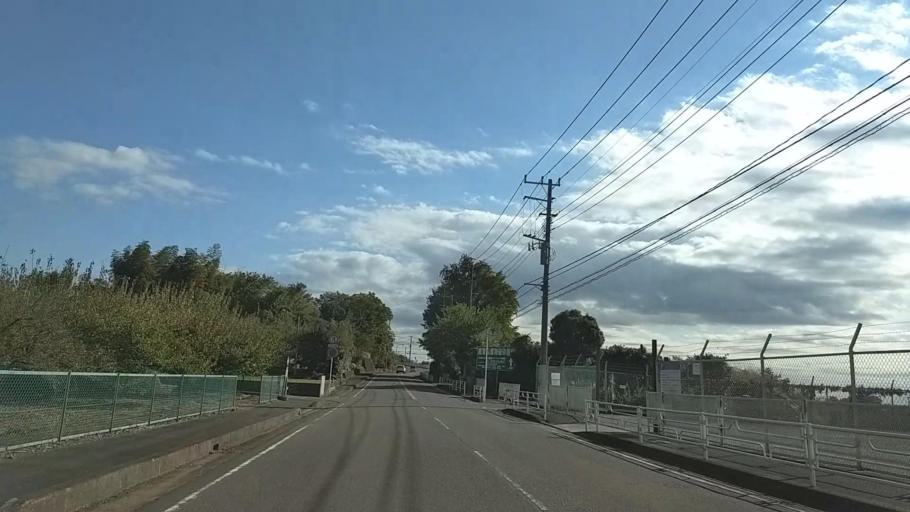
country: JP
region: Kanagawa
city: Odawara
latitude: 35.3106
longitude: 139.1775
